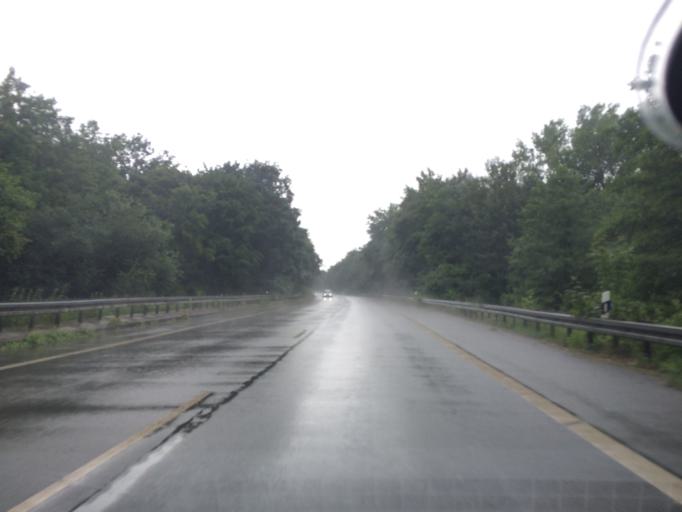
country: DE
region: North Rhine-Westphalia
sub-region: Regierungsbezirk Munster
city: Haltern
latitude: 51.7725
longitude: 7.2345
